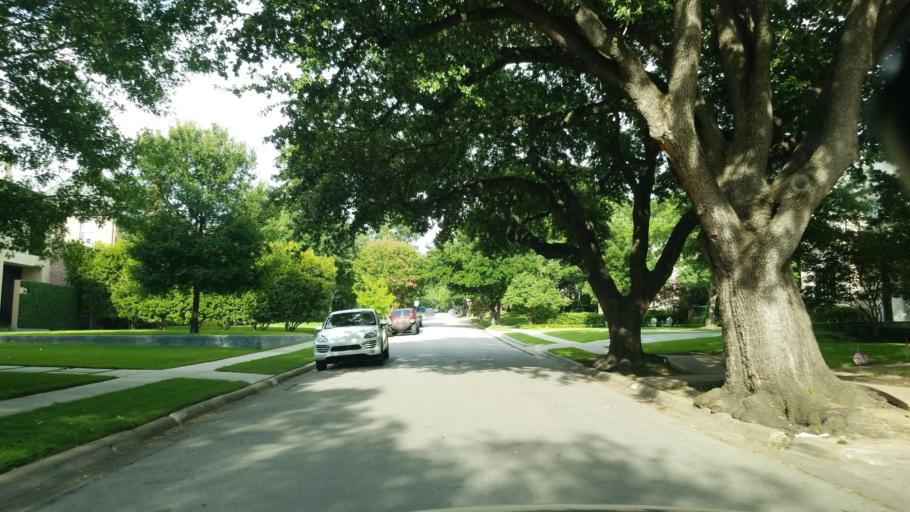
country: US
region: Texas
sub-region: Dallas County
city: University Park
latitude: 32.8530
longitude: -96.7783
